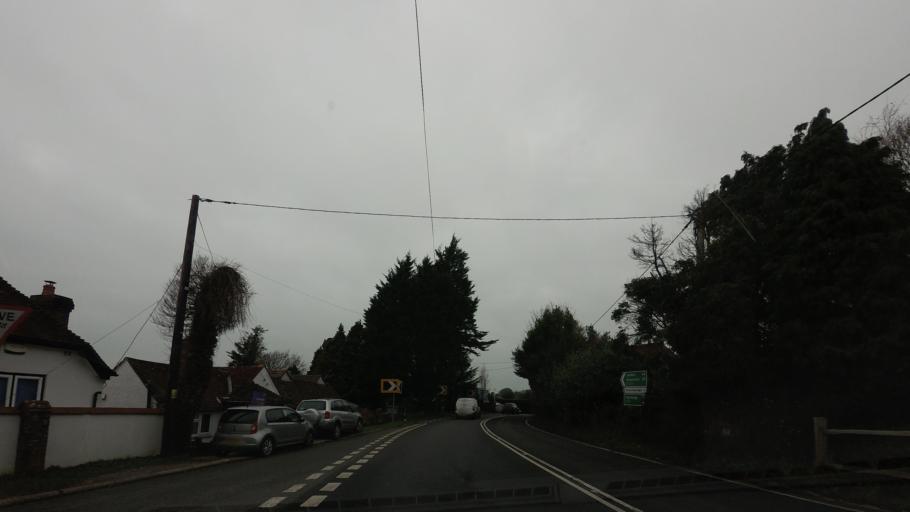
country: GB
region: England
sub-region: East Sussex
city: Battle
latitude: 50.9457
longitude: 0.5087
